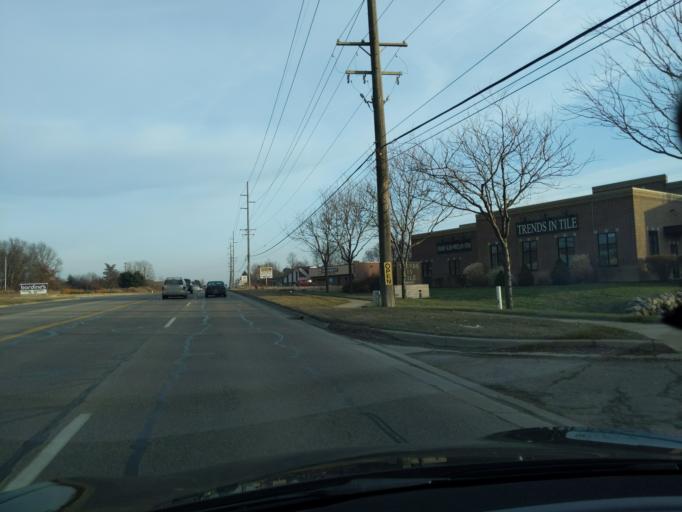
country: US
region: Michigan
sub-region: Livingston County
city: Brighton
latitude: 42.5724
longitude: -83.8270
